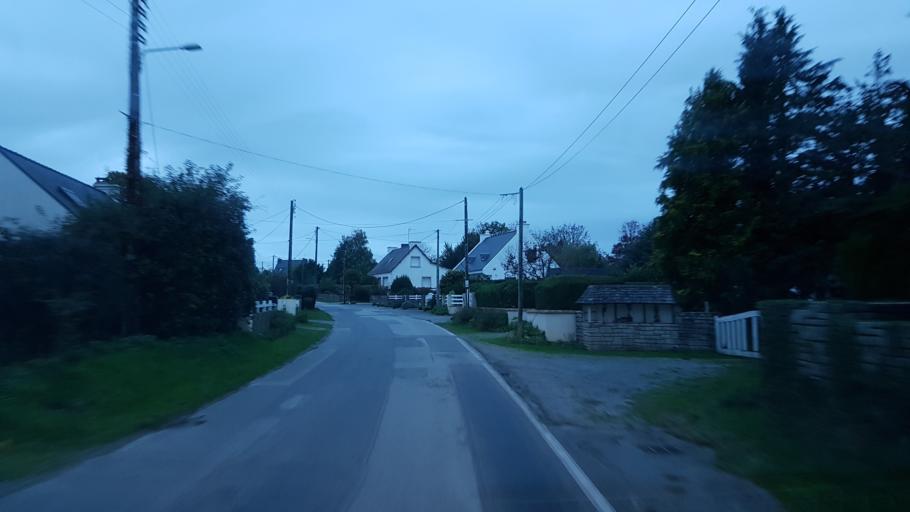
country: FR
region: Brittany
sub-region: Departement du Morbihan
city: Sarzeau
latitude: 47.5420
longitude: -2.7840
